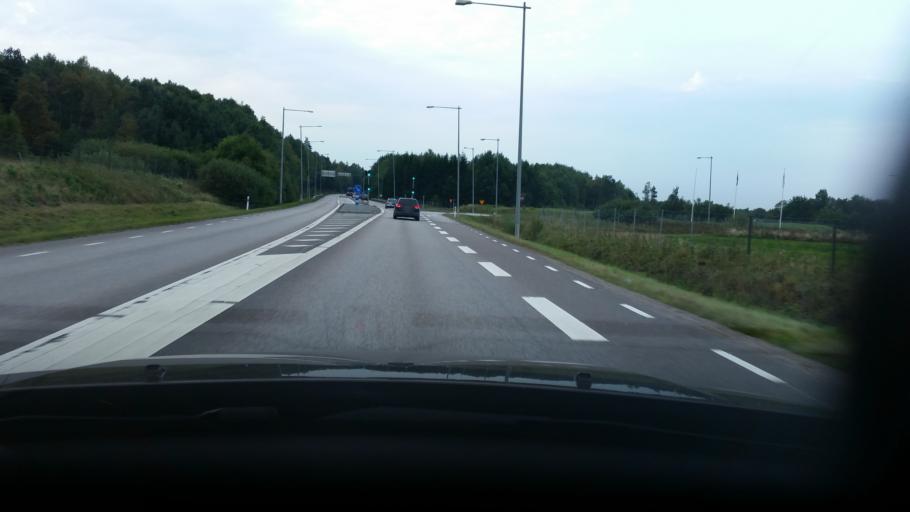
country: SE
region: Vaestra Goetaland
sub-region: Goteborg
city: Majorna
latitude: 57.7677
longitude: 11.8856
